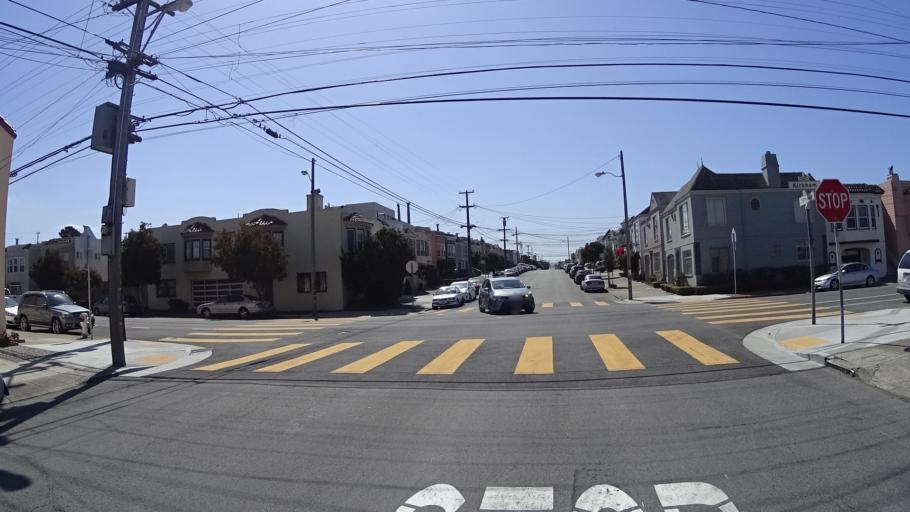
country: US
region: California
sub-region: San Mateo County
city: Daly City
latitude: 37.7596
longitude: -122.4876
